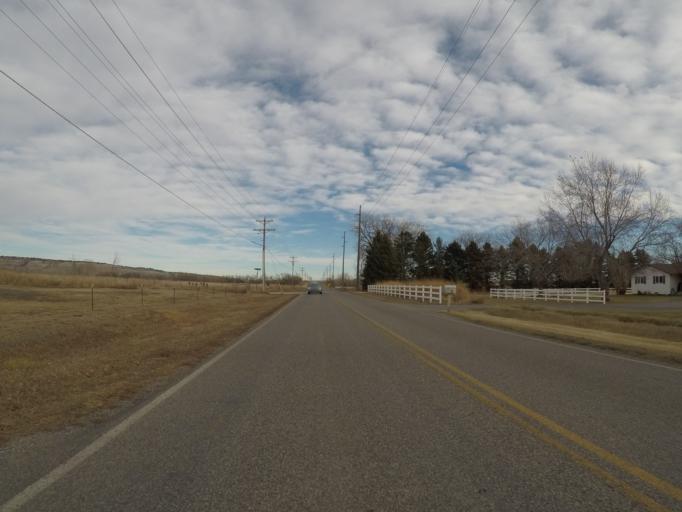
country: US
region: Montana
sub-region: Yellowstone County
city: Laurel
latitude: 45.7841
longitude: -108.6848
